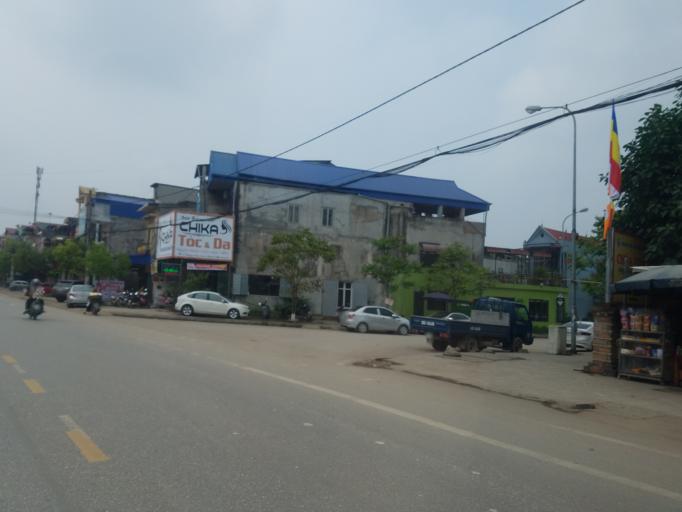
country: VN
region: Thai Nguyen
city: Chua Hang
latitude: 21.6219
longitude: 105.8420
